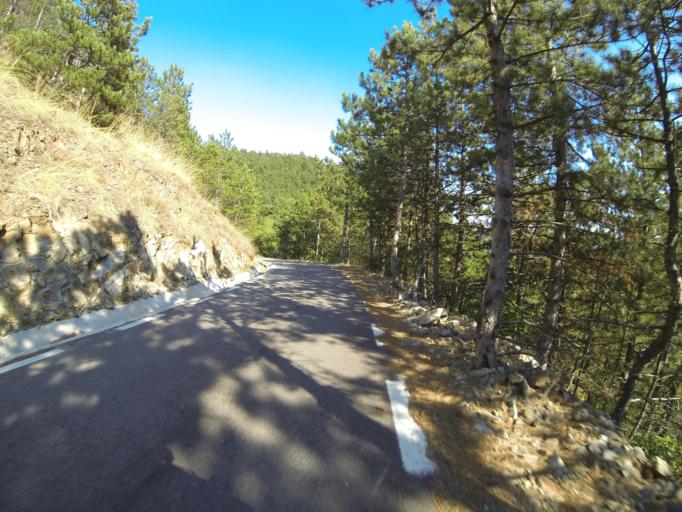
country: RO
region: Mehedinti
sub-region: Comuna Svinita
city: Svinita
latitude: 44.5421
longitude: 22.1876
